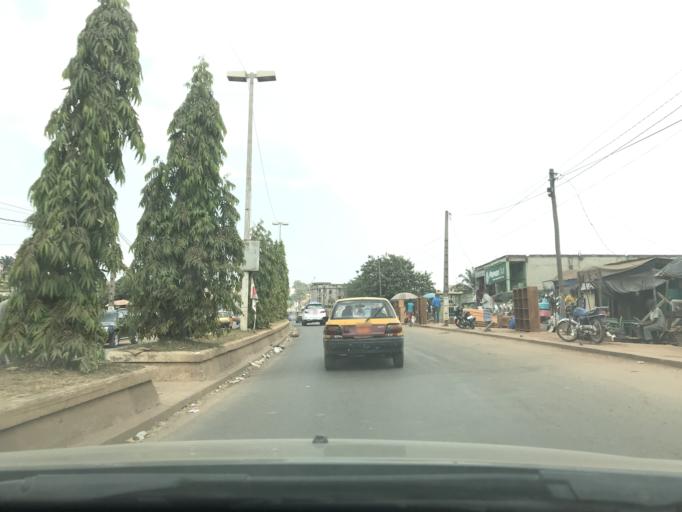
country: CM
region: Centre
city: Yaounde
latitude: 3.8868
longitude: 11.5281
